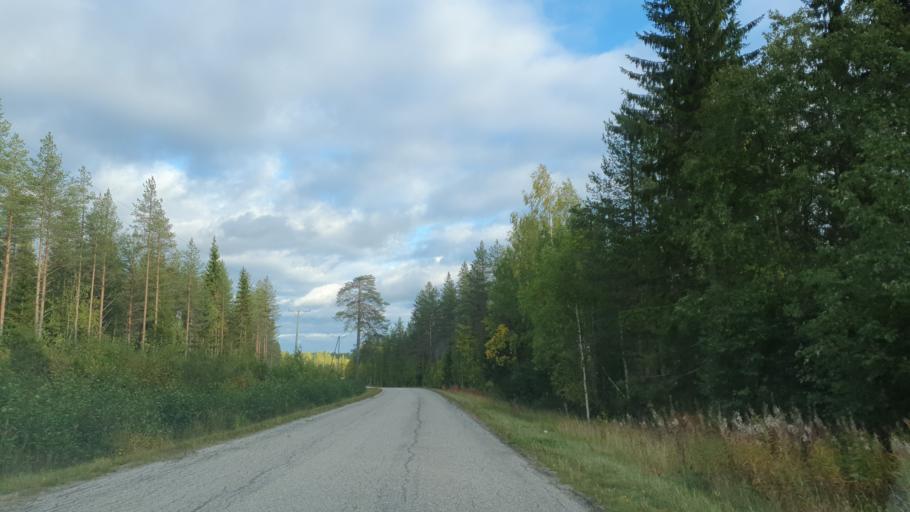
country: FI
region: Kainuu
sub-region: Kehys-Kainuu
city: Kuhmo
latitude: 63.9224
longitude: 30.0452
